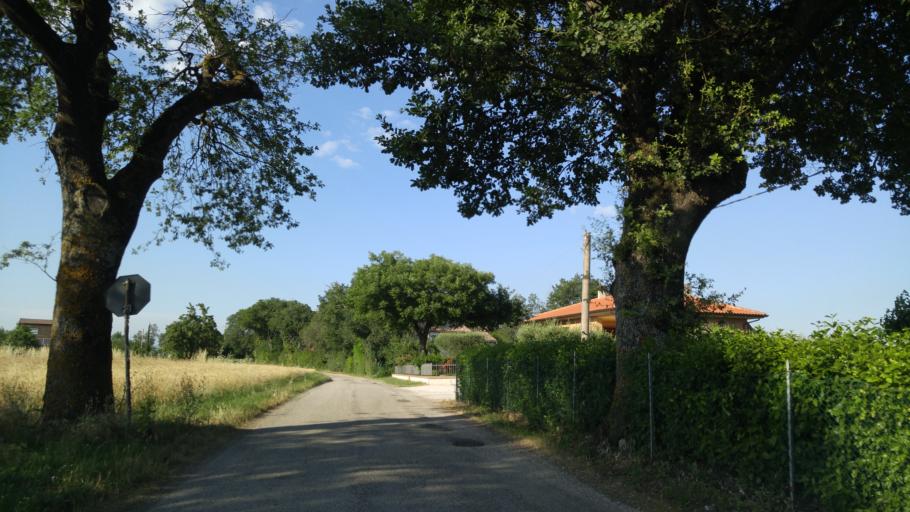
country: IT
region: The Marches
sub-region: Provincia di Pesaro e Urbino
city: Sant'Ippolito
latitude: 43.6964
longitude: 12.8761
